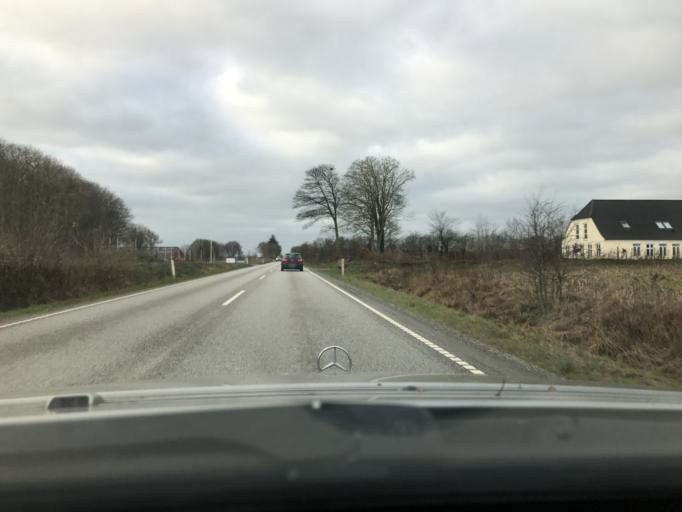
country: DK
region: South Denmark
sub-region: Aabenraa Kommune
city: Rodekro
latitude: 55.0748
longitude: 9.2801
